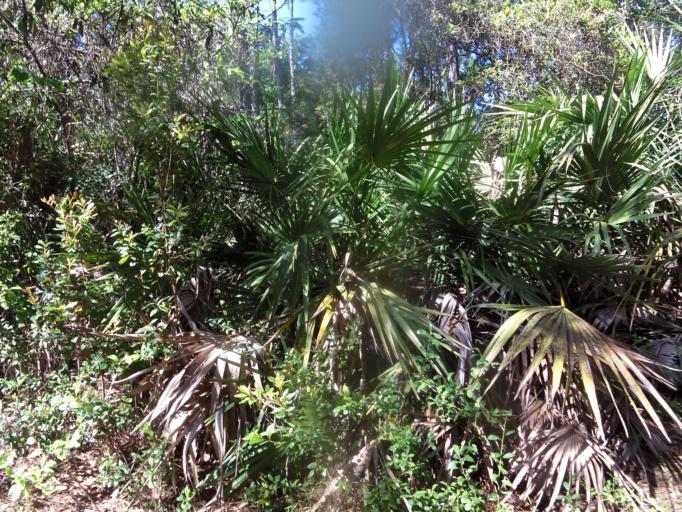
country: US
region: Florida
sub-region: Duval County
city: Atlantic Beach
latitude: 30.4506
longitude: -81.4813
